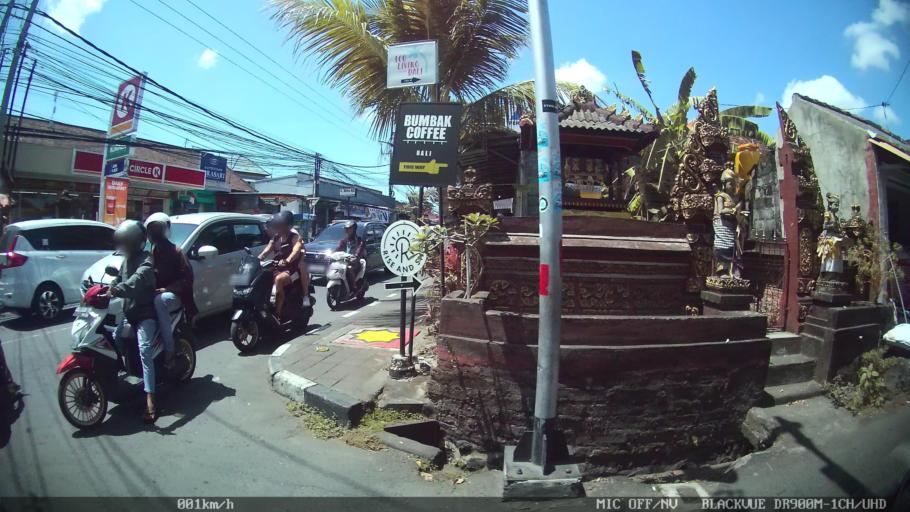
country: ID
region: Bali
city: Banjar Gunungpande
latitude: -8.6455
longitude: 115.1602
